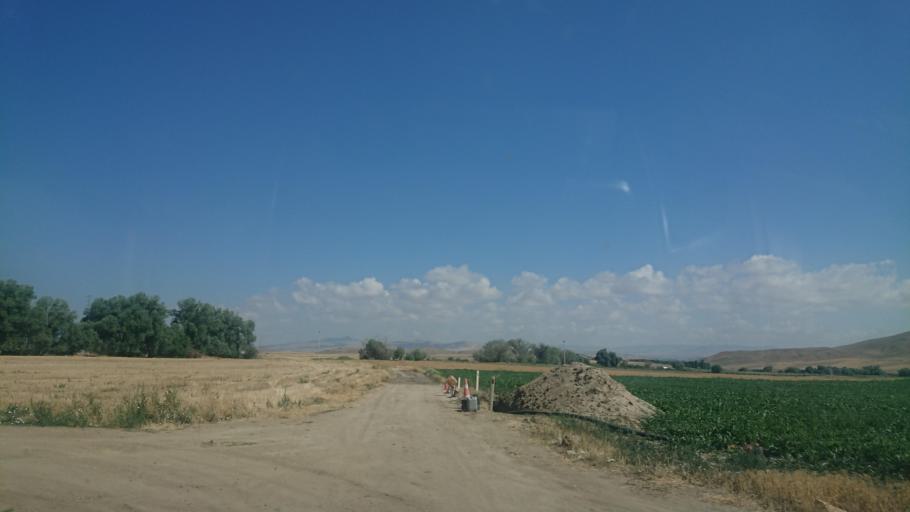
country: TR
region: Aksaray
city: Sariyahsi
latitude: 38.9959
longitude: 33.8949
